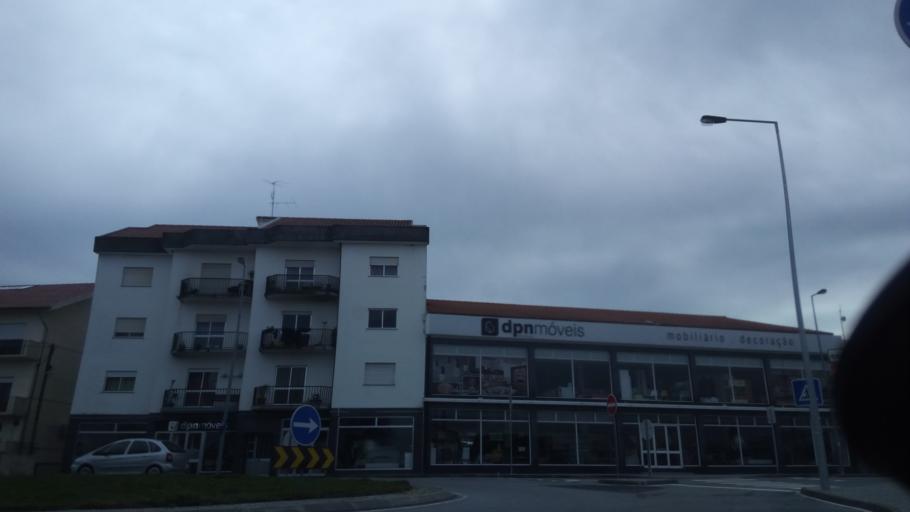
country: PT
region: Guarda
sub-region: Seia
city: Seia
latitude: 40.4135
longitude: -7.7106
